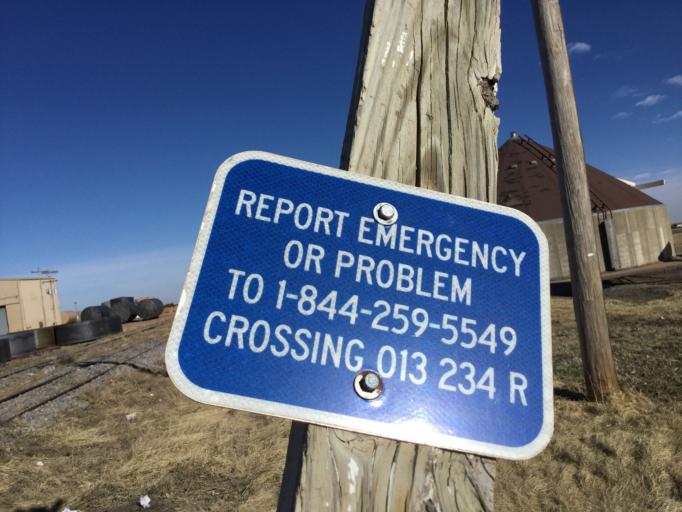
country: US
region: Kansas
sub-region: Stevens County
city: Hugoton
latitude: 37.1228
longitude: -101.6278
